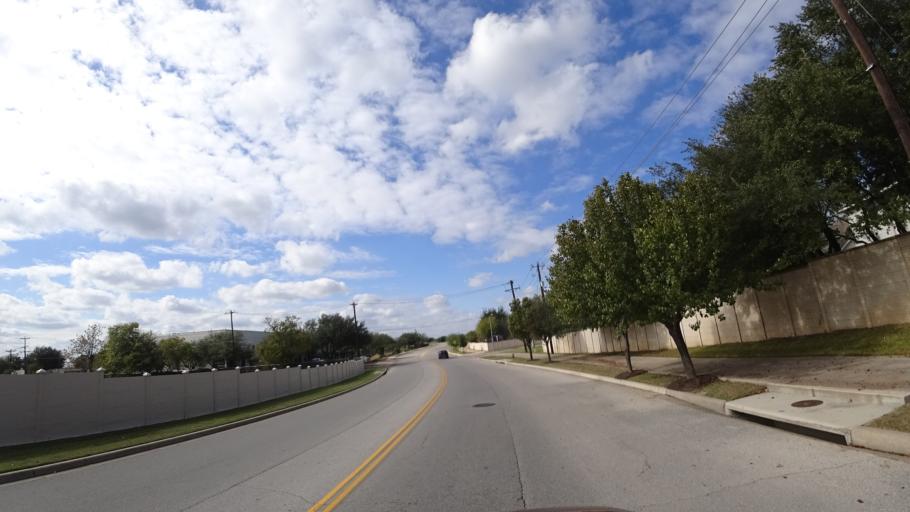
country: US
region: Texas
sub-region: Travis County
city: Windemere
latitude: 30.4382
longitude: -97.6436
